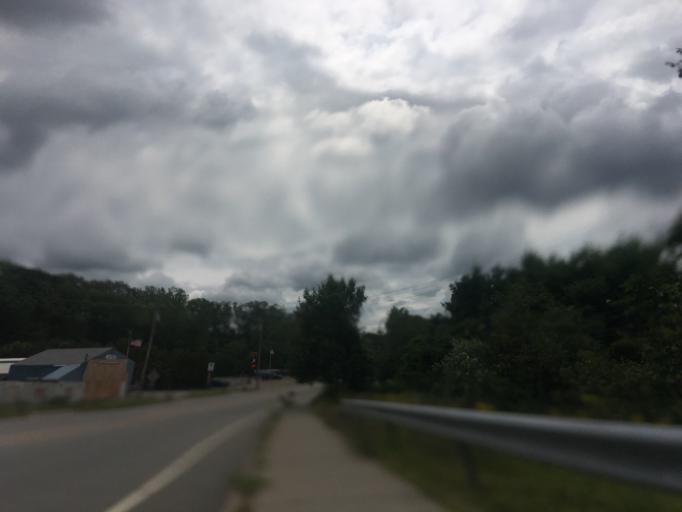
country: US
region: Connecticut
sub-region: Windham County
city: Danielson
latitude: 41.7959
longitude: -71.8848
